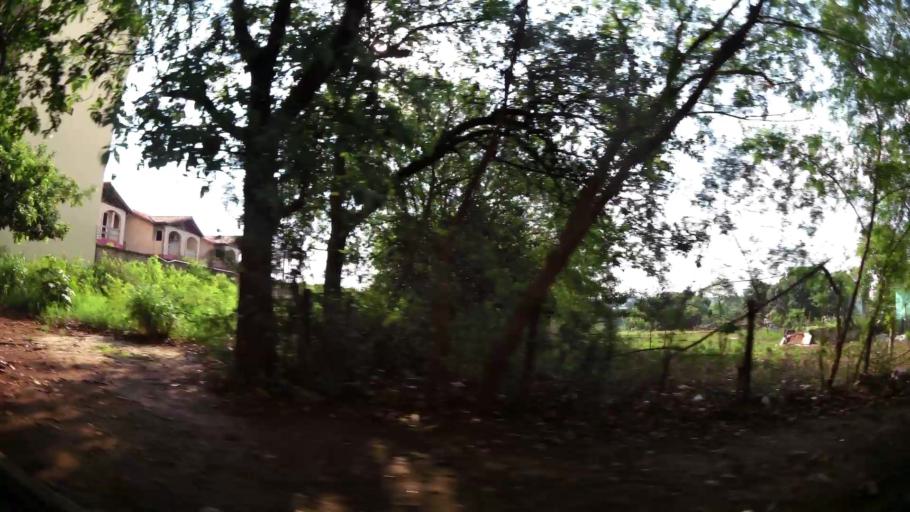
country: PY
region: Alto Parana
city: Presidente Franco
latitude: -25.5299
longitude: -54.6268
